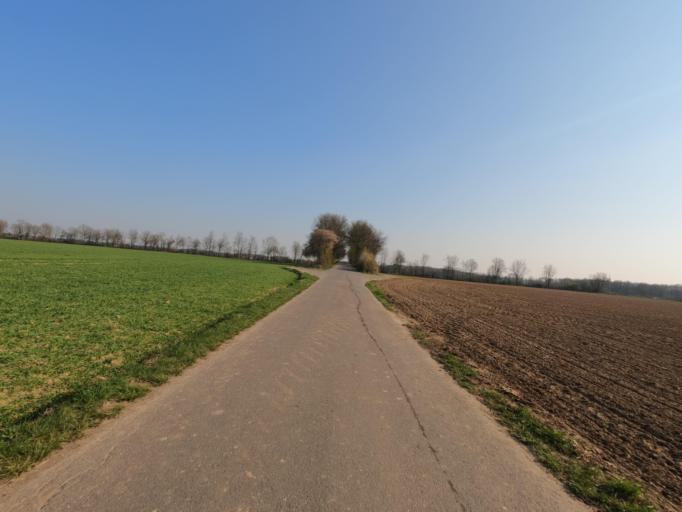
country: DE
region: North Rhine-Westphalia
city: Huckelhoven
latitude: 51.0682
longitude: 6.2606
